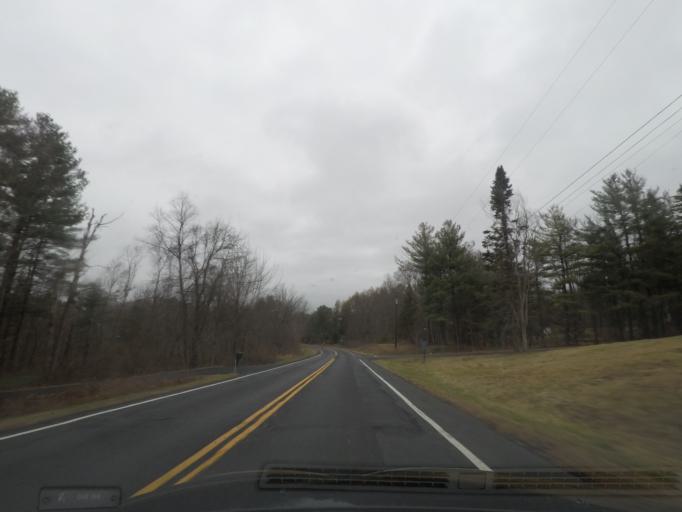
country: US
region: New York
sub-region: Rensselaer County
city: East Greenbush
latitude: 42.6007
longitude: -73.6477
